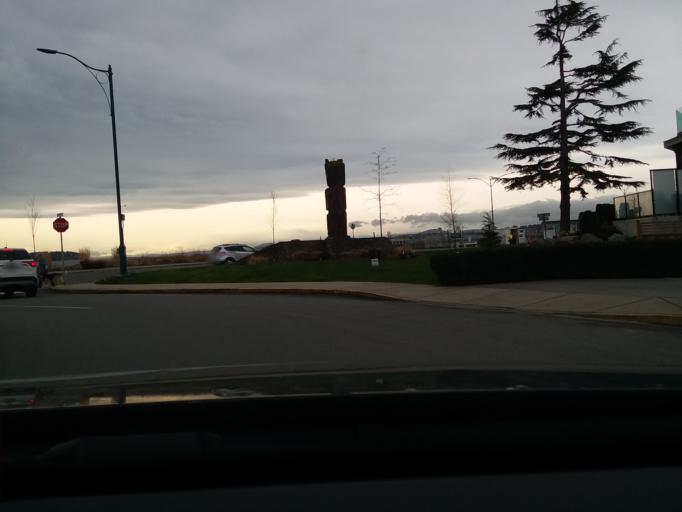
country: CA
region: British Columbia
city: North Saanich
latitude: 48.6451
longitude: -123.3965
